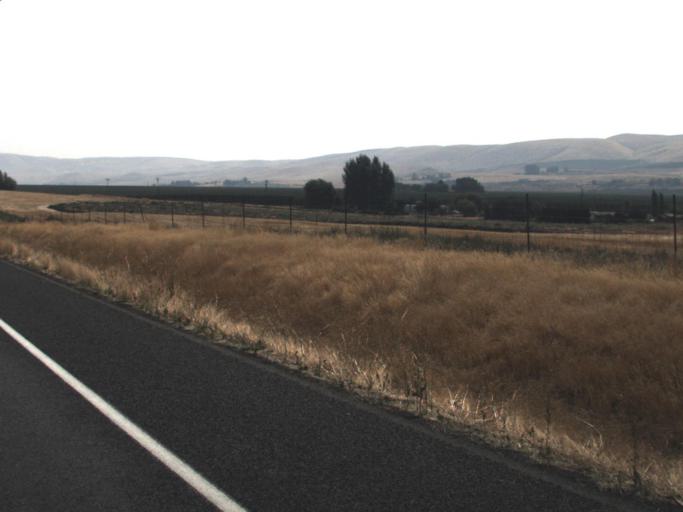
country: US
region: Washington
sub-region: Yakima County
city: Zillah
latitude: 46.5227
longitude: -120.2413
